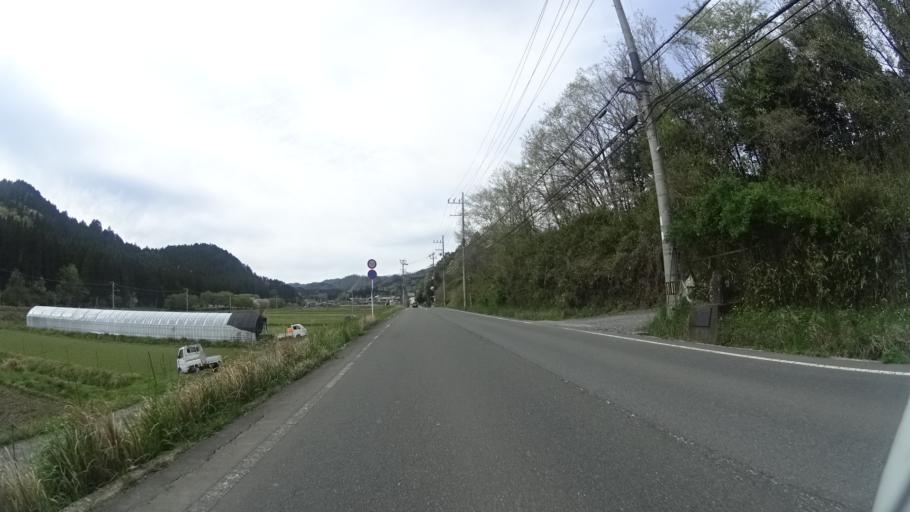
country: JP
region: Kyoto
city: Kameoka
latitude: 35.1874
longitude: 135.4838
